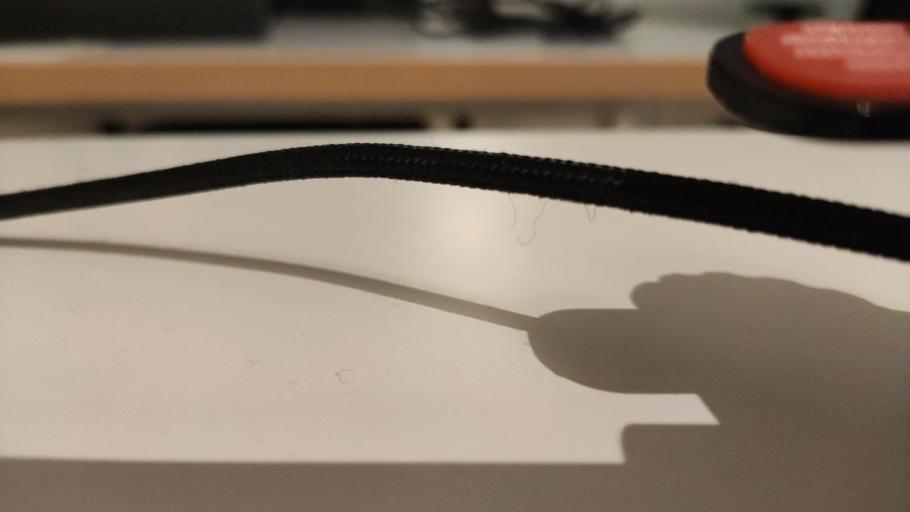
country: RU
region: Moskovskaya
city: Rogachevo
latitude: 56.4320
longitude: 37.1808
